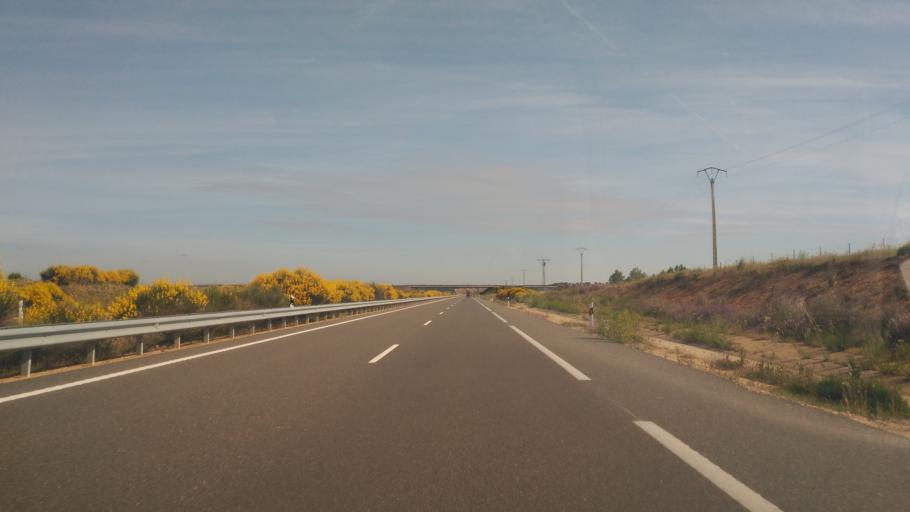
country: ES
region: Castille and Leon
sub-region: Provincia de Salamanca
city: Topas
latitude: 41.1957
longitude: -5.6987
